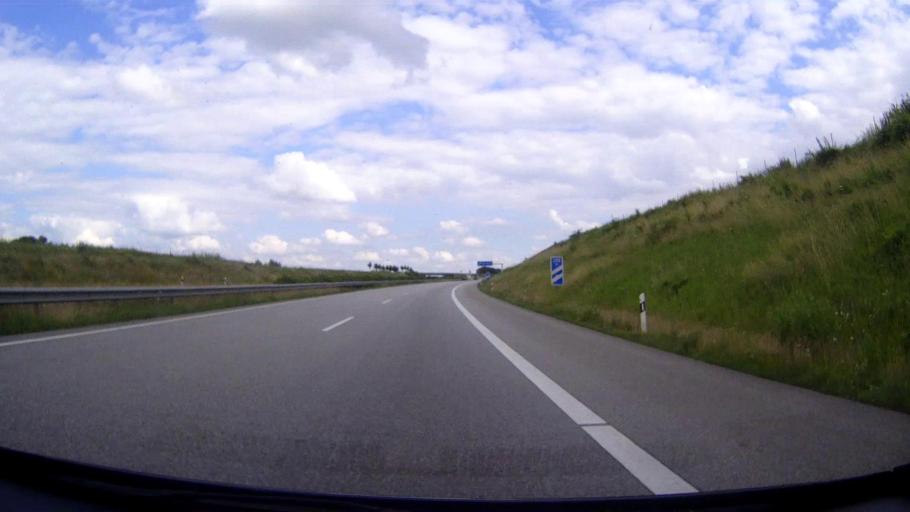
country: DE
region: Schleswig-Holstein
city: Geschendorf
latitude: 53.9244
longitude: 10.4481
